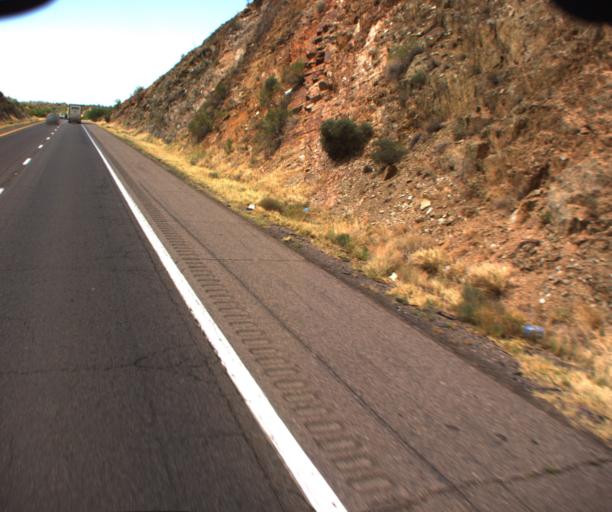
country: US
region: Arizona
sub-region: Maricopa County
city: New River
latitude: 33.9467
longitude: -112.1403
